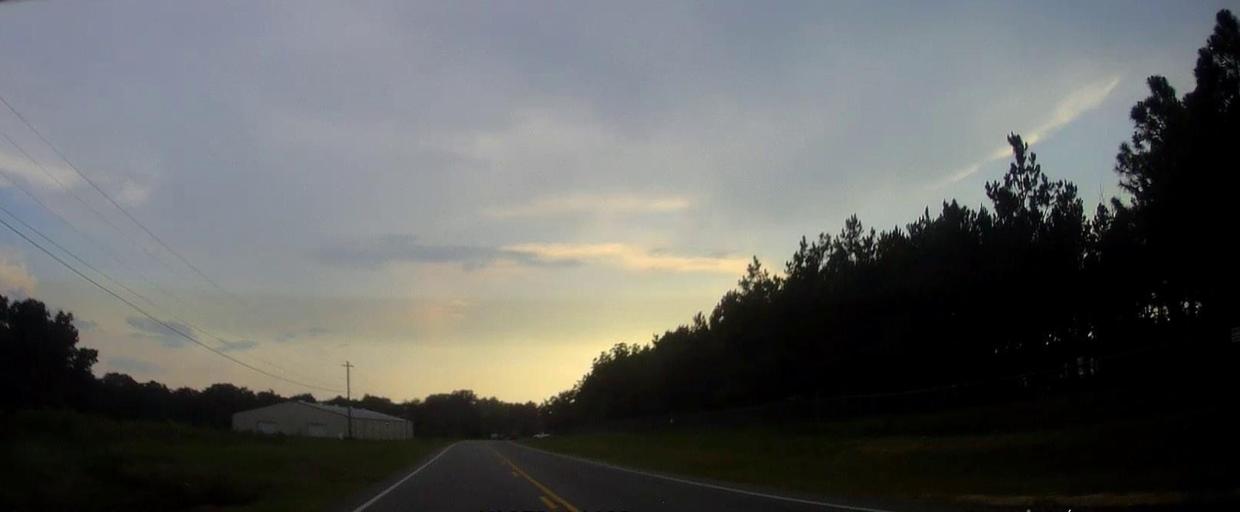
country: US
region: Georgia
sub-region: Laurens County
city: East Dublin
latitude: 32.5507
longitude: -82.8507
